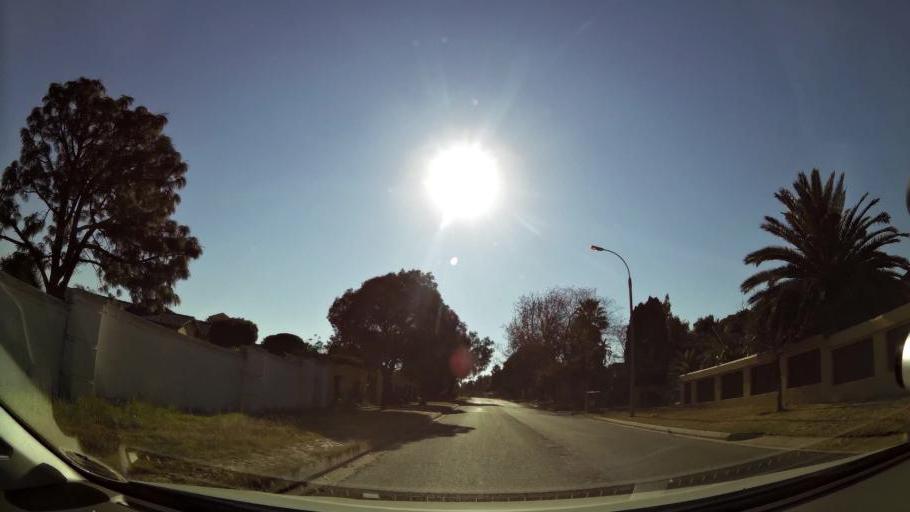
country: ZA
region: Gauteng
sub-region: City of Johannesburg Metropolitan Municipality
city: Modderfontein
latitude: -26.0586
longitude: 28.1995
